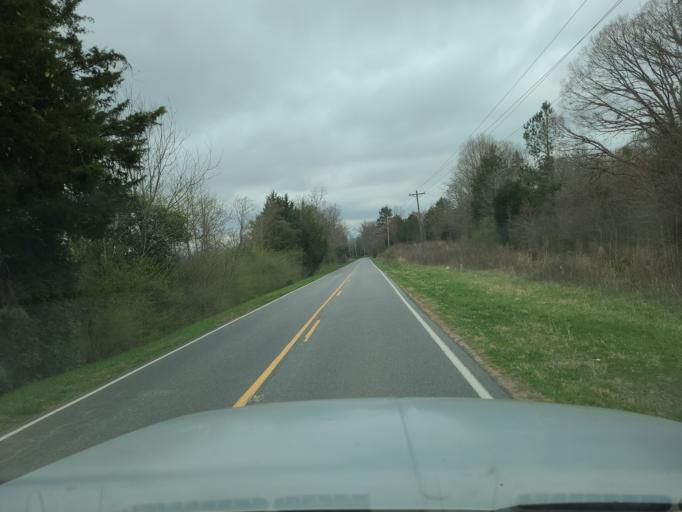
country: US
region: North Carolina
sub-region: Cleveland County
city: Shelby
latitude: 35.4357
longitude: -81.6416
